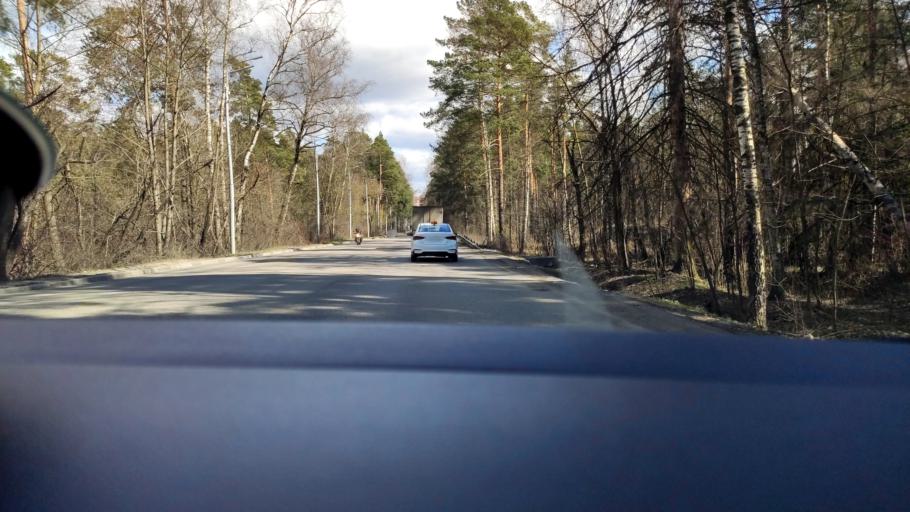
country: RU
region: Moscow
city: Vostochnyy
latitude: 55.8267
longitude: 37.9023
